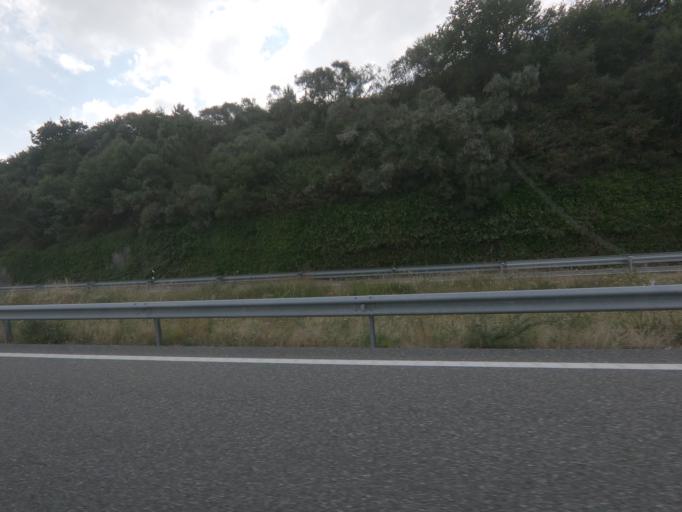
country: ES
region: Galicia
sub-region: Provincia de Ourense
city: Melon
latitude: 42.2388
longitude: -8.2287
